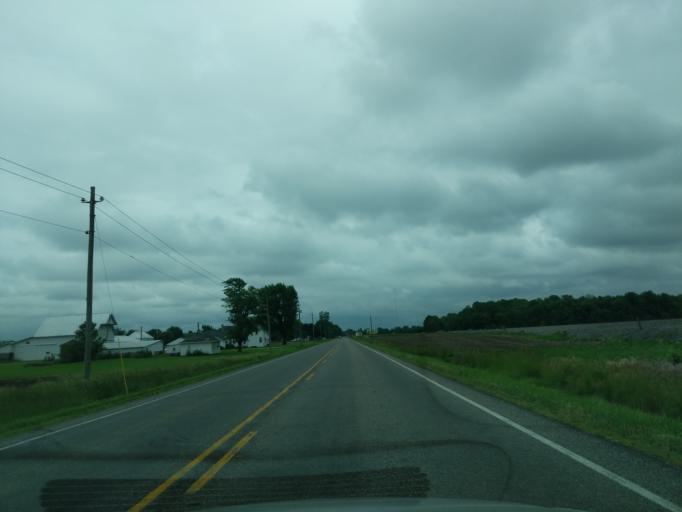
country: US
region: Indiana
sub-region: Madison County
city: Elwood
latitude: 40.2768
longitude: -85.8759
